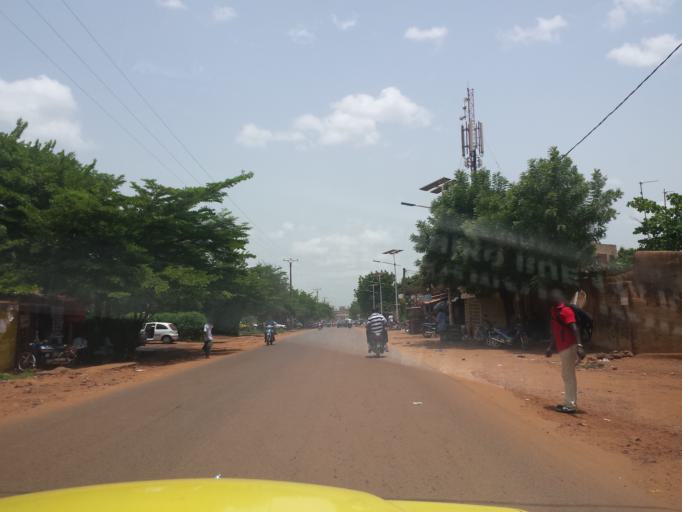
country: ML
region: Bamako
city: Bamako
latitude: 12.6052
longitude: -7.9617
